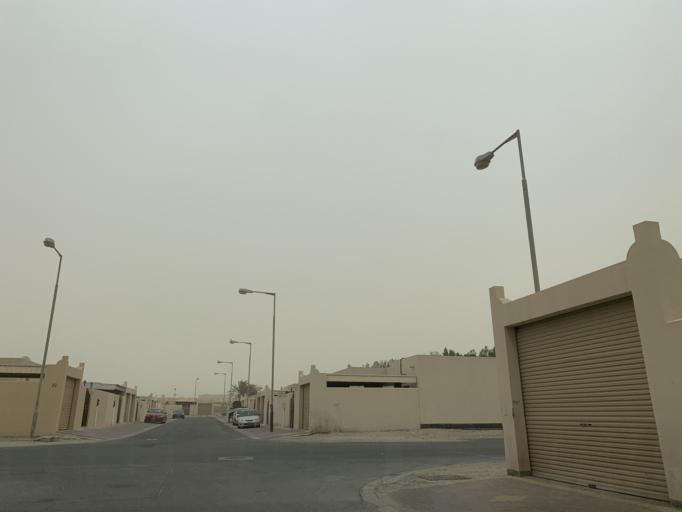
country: BH
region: Central Governorate
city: Madinat Hamad
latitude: 26.1318
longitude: 50.5242
